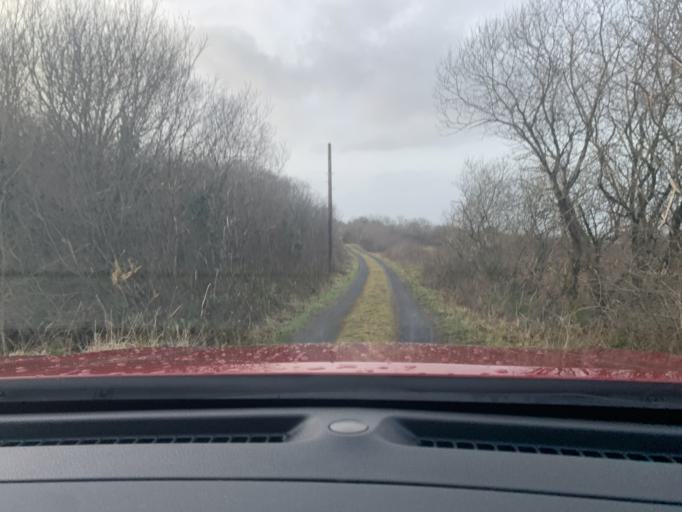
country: IE
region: Connaught
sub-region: Roscommon
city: Ballaghaderreen
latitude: 53.9516
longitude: -8.5341
